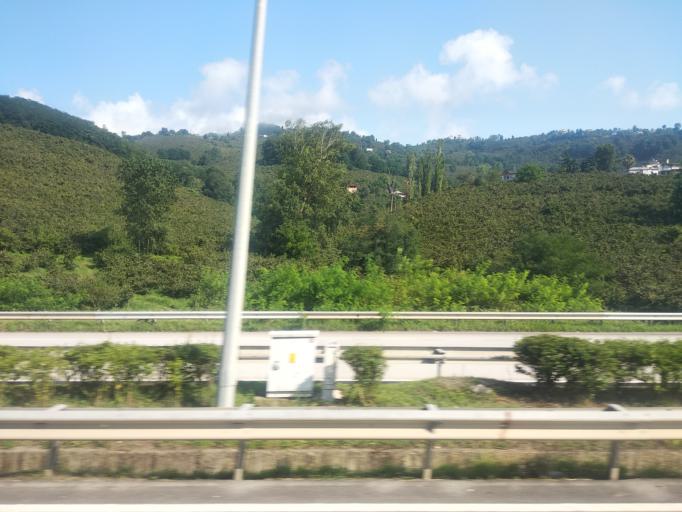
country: TR
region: Ordu
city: Ordu
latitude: 41.0093
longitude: 37.8311
